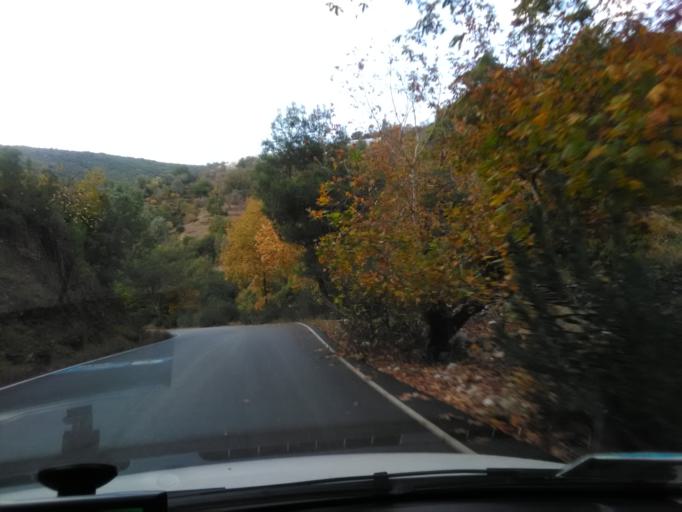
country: TR
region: Antalya
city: Gazipasa
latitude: 36.2845
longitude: 32.3687
